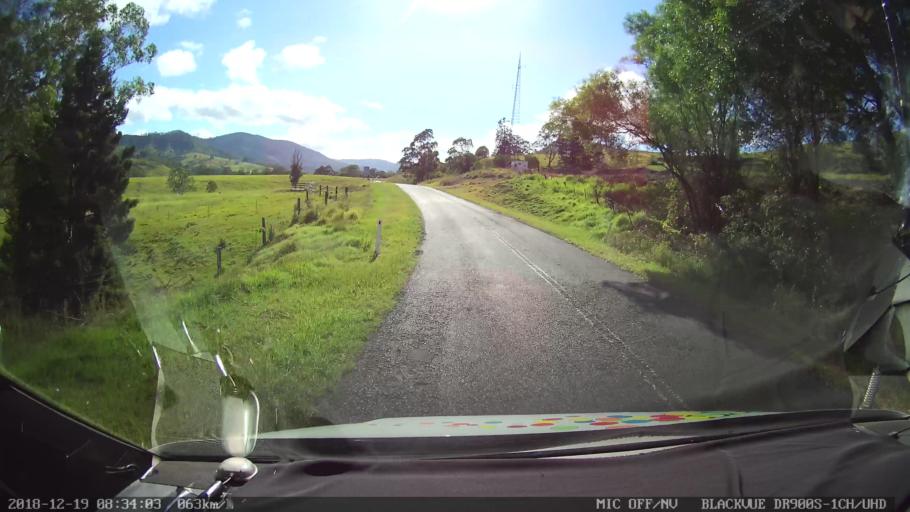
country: AU
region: New South Wales
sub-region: Kyogle
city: Kyogle
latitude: -28.3210
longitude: 152.9561
